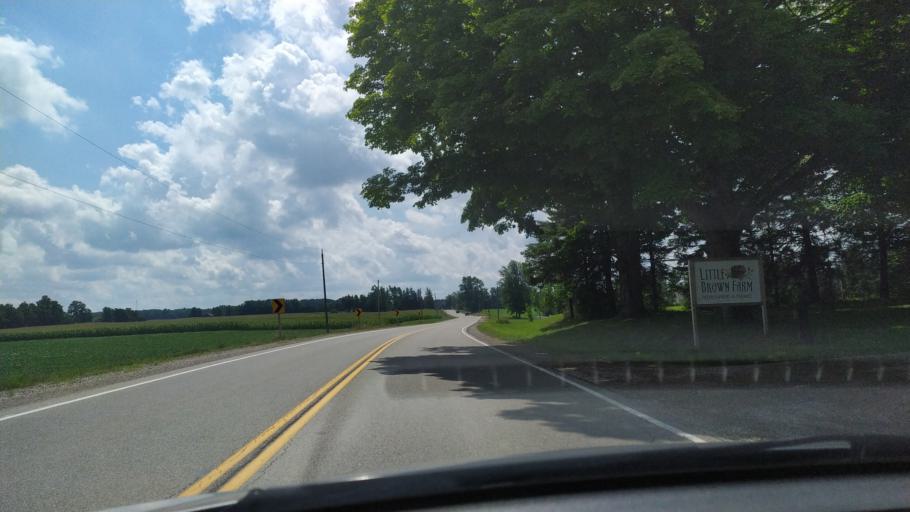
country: CA
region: Ontario
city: London
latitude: 43.0613
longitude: -81.3326
